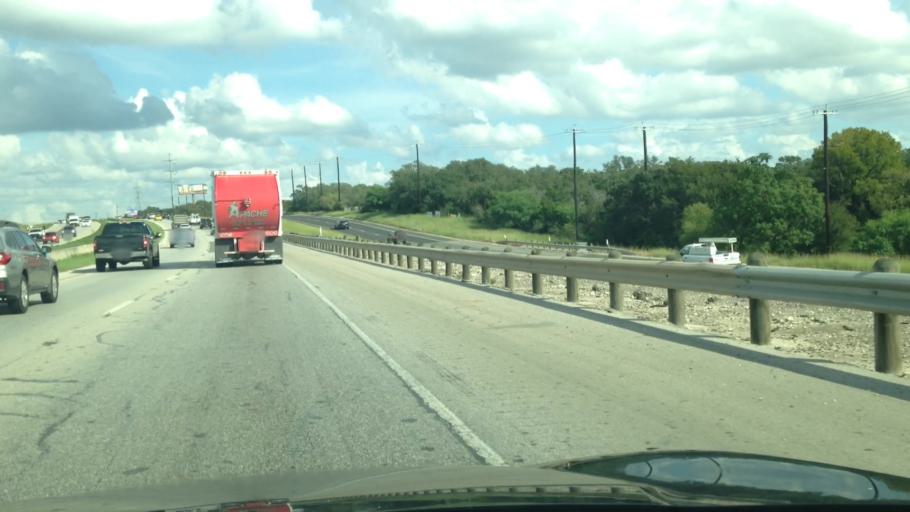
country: US
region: Texas
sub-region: Bexar County
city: Hollywood Park
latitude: 29.6000
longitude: -98.4339
